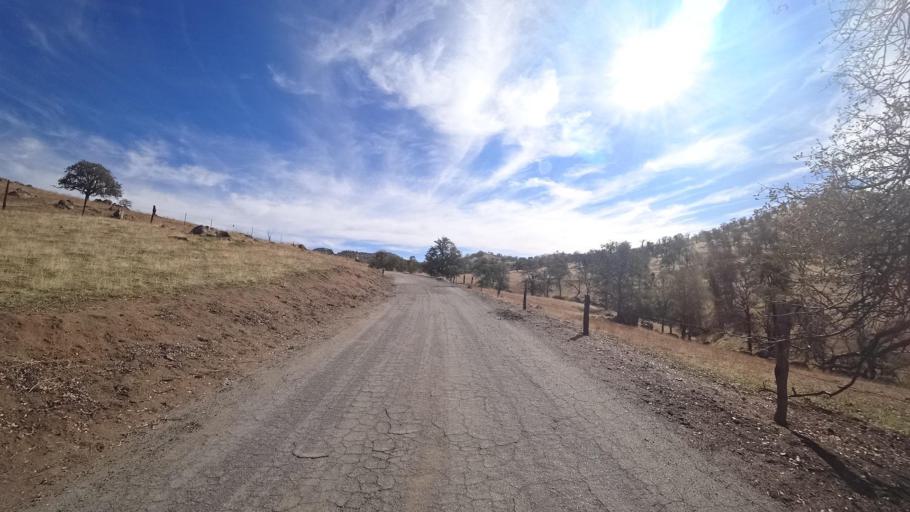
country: US
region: California
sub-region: Kern County
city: Oildale
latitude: 35.5752
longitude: -118.8099
